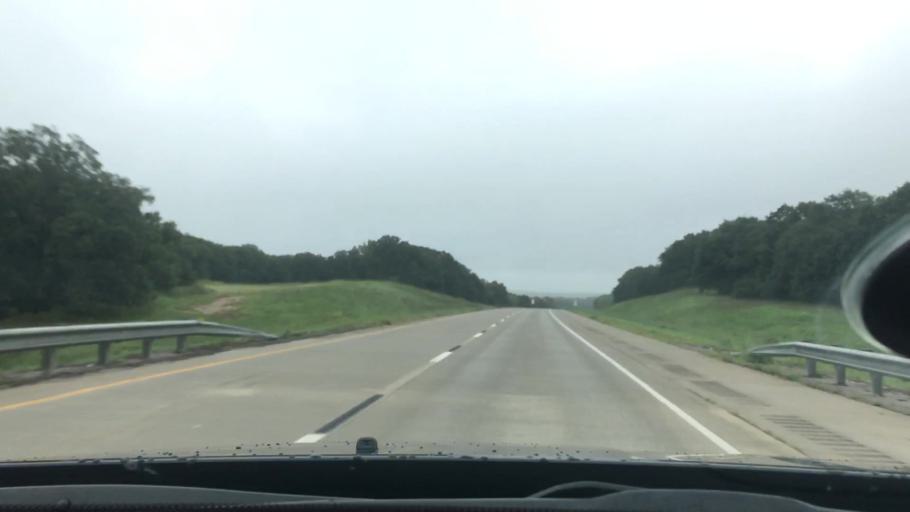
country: US
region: Oklahoma
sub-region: Okfuskee County
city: Boley
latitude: 35.3838
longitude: -96.5650
